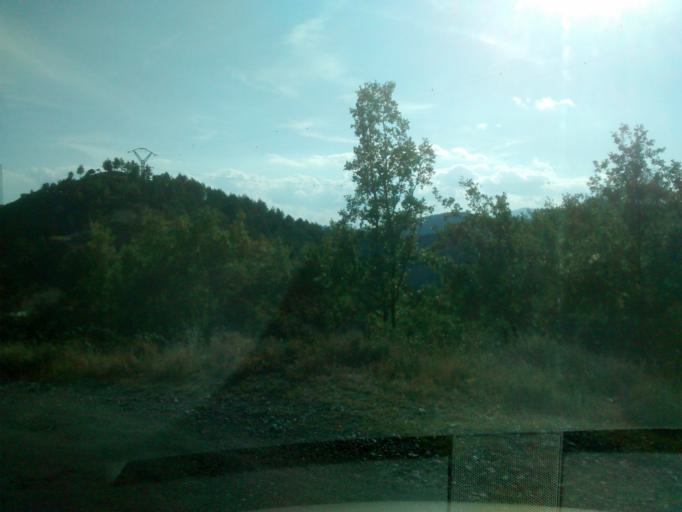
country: ES
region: Aragon
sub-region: Provincia de Huesca
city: Puertolas
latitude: 42.5635
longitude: 0.1718
